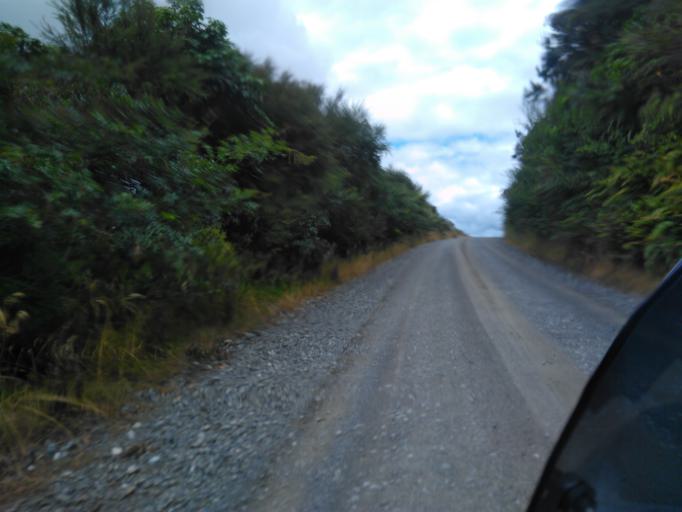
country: NZ
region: Gisborne
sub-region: Gisborne District
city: Gisborne
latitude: -38.1638
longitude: 178.1361
